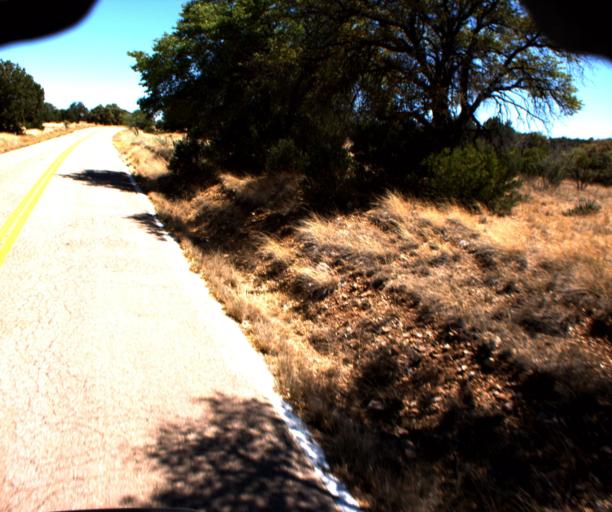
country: US
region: Arizona
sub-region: Cochise County
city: Huachuca City
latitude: 31.5589
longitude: -110.5531
